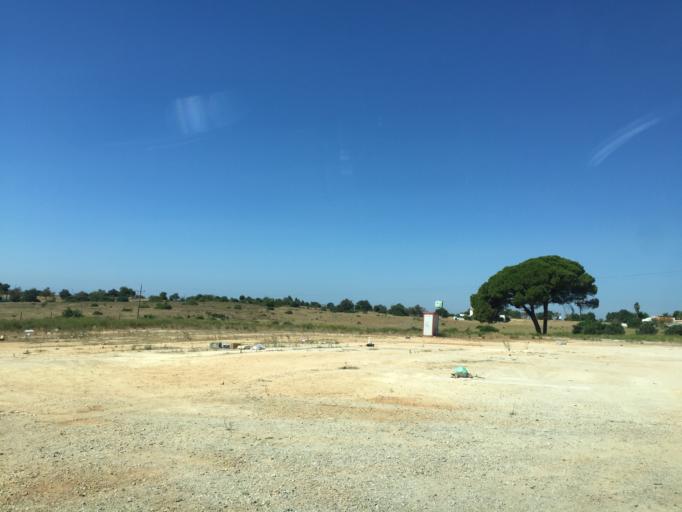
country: PT
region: Faro
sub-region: Albufeira
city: Ferreiras
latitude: 37.1229
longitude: -8.2453
